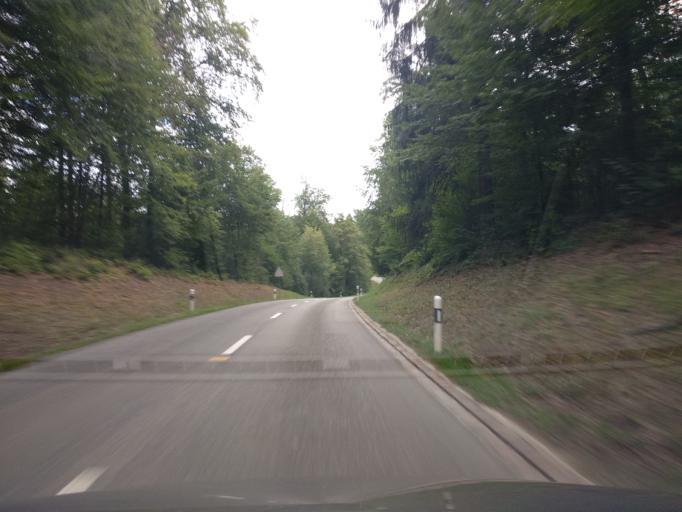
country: CH
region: Thurgau
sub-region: Frauenfeld District
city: Diessenhofen
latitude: 47.6754
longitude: 8.7194
